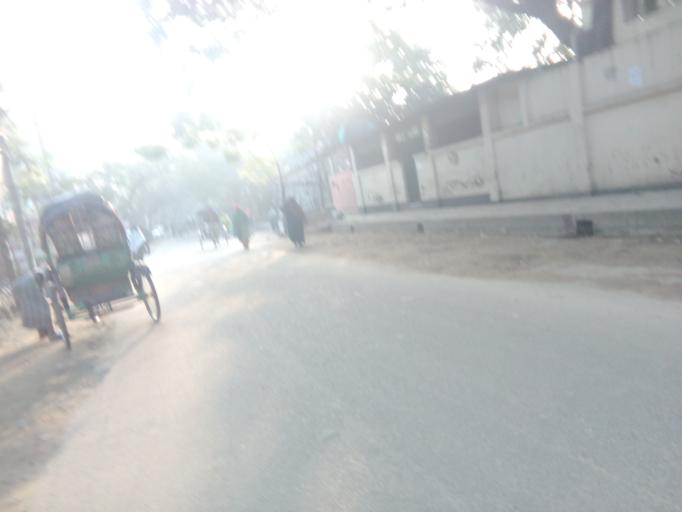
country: BD
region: Dhaka
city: Paltan
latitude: 23.7505
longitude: 90.4226
